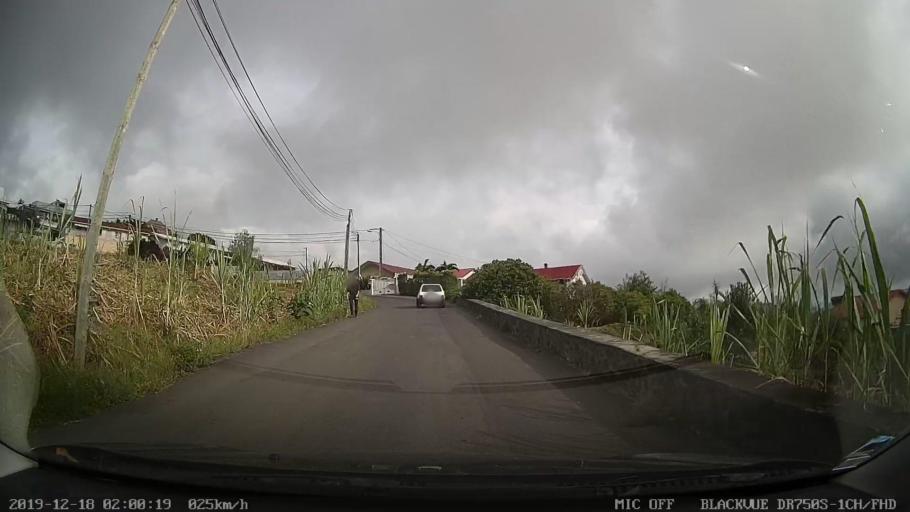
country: RE
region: Reunion
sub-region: Reunion
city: Le Tampon
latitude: -21.2539
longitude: 55.5174
